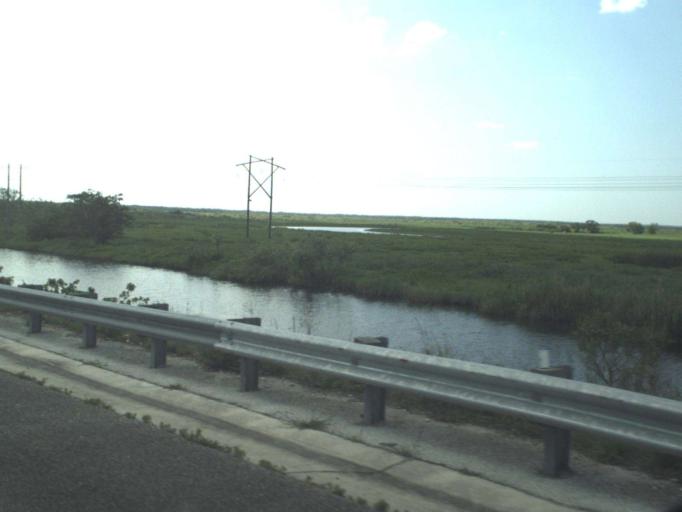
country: US
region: Florida
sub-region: Brevard County
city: Cocoa West
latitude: 28.3698
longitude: -80.8760
